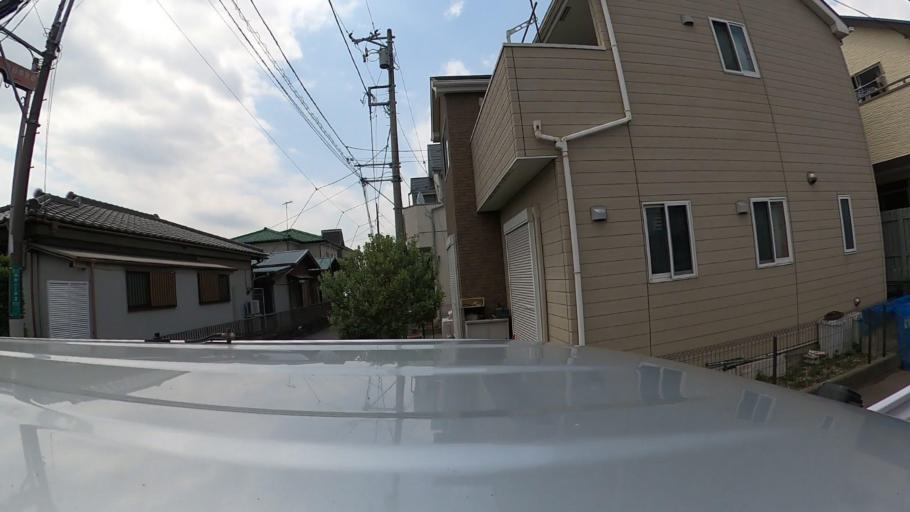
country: JP
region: Kanagawa
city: Chigasaki
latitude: 35.3752
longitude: 139.3959
